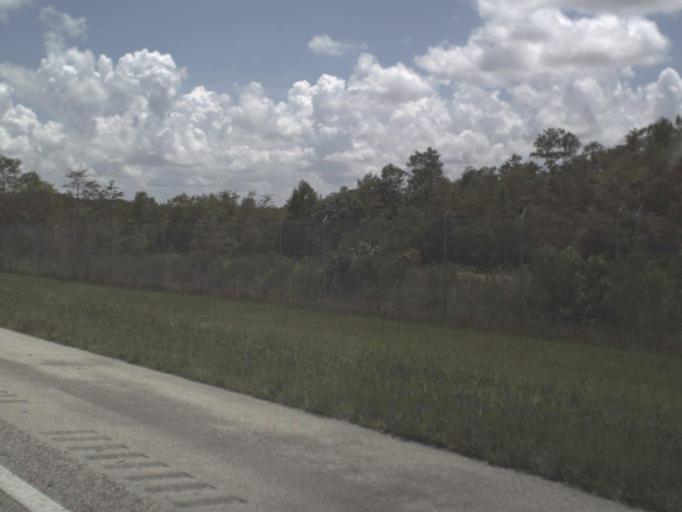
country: US
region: Florida
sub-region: Collier County
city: Immokalee
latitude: 26.1710
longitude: -80.9511
